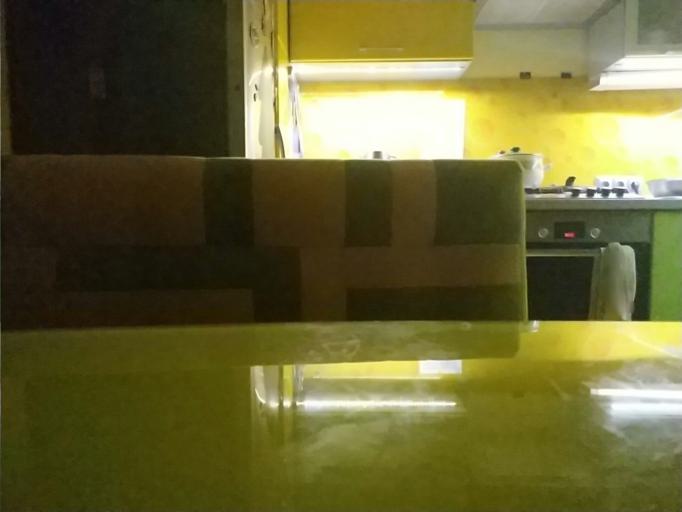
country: RU
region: Republic of Karelia
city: Pyaozerskiy
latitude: 65.6127
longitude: 30.5585
